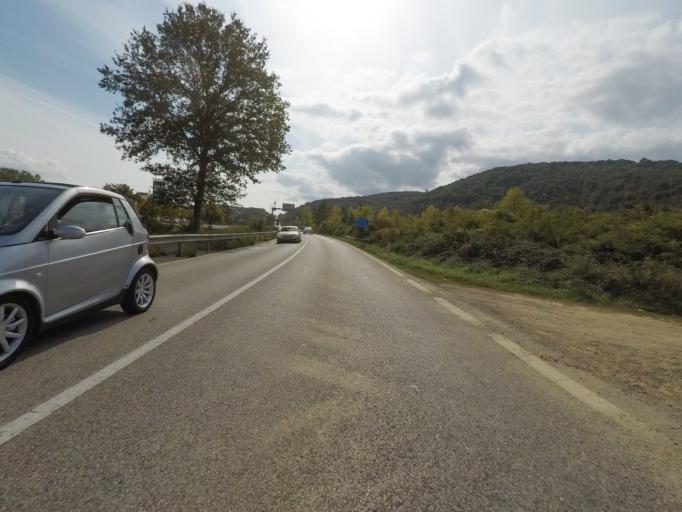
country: IT
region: Tuscany
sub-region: Provincia di Siena
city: Murlo
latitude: 43.1470
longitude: 11.2860
